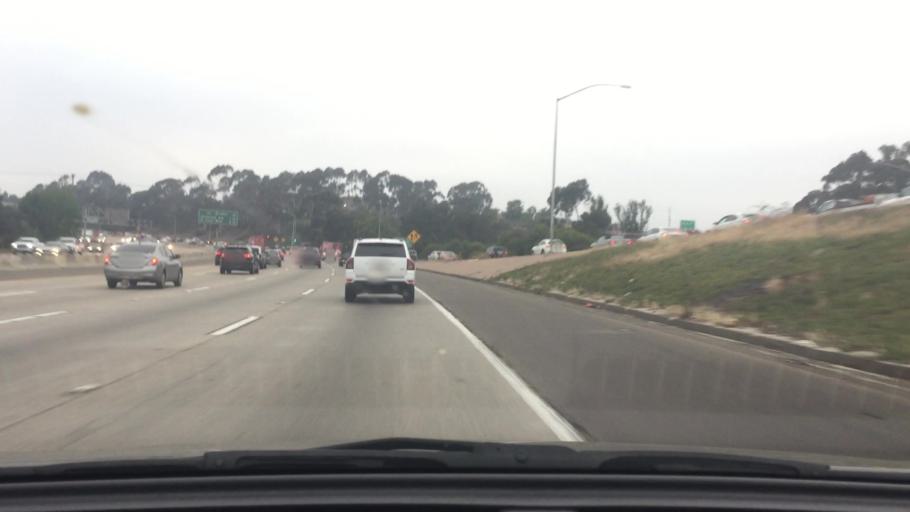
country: US
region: California
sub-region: San Diego County
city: National City
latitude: 32.7237
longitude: -117.1025
